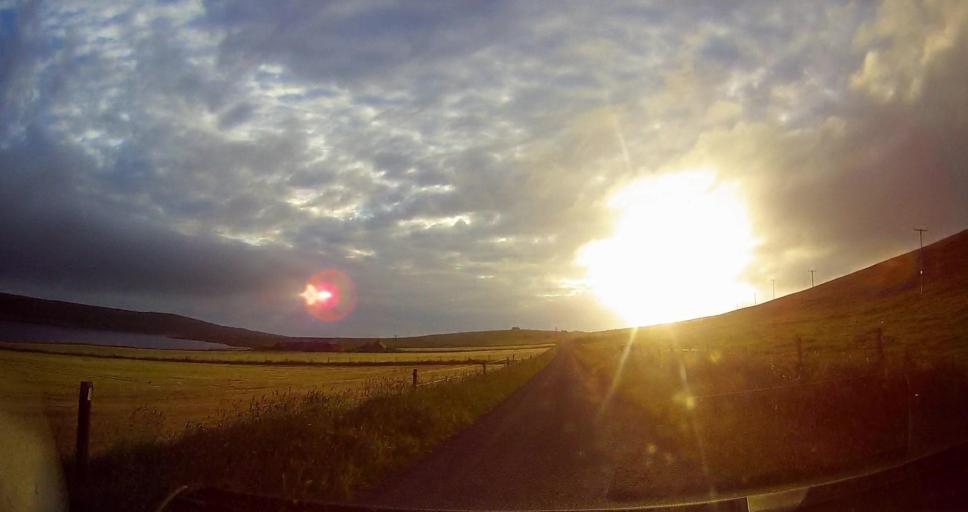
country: GB
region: Scotland
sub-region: Orkney Islands
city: Stromness
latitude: 59.1178
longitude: -3.2638
